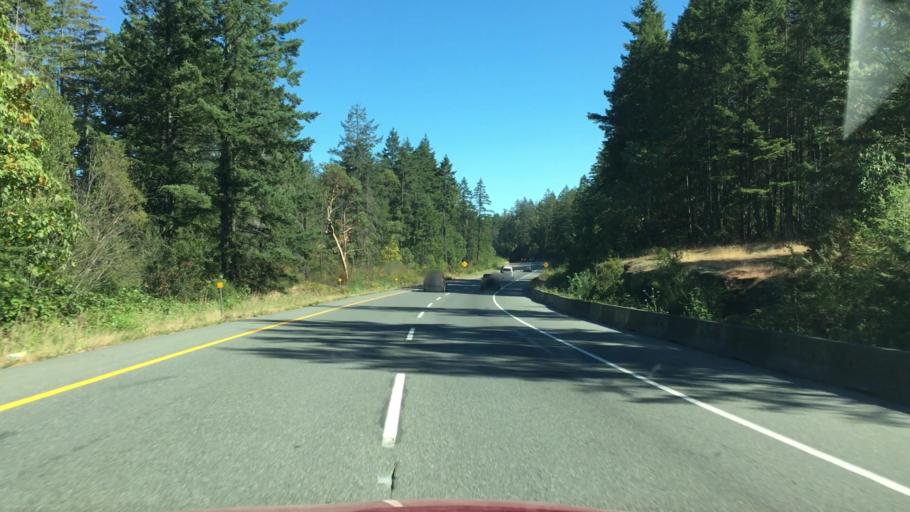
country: CA
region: British Columbia
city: Nanaimo
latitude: 49.1389
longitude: -123.9580
